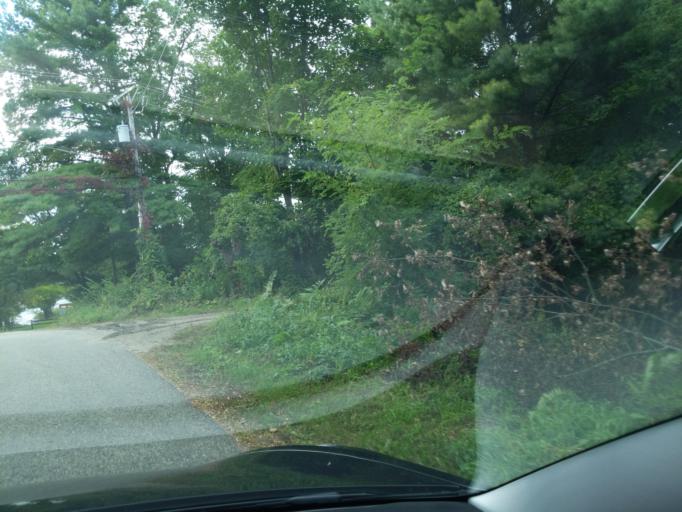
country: US
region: Michigan
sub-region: Kalkaska County
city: Rapid City
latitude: 44.8885
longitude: -85.2738
